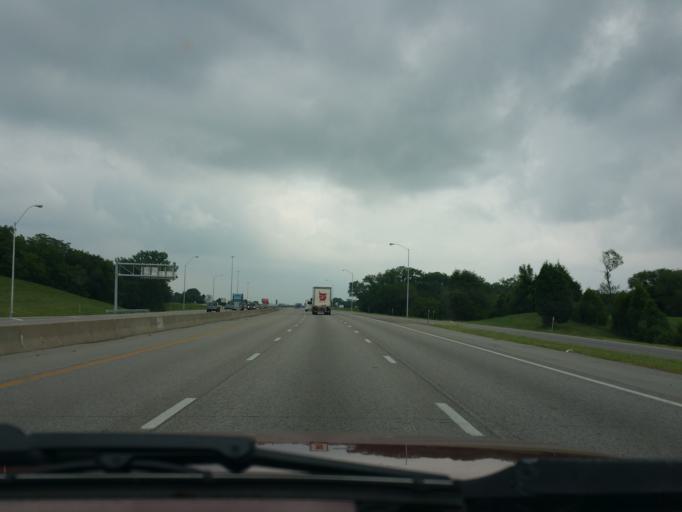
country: US
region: Kansas
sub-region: Johnson County
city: Shawnee
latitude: 39.1051
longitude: -94.7577
